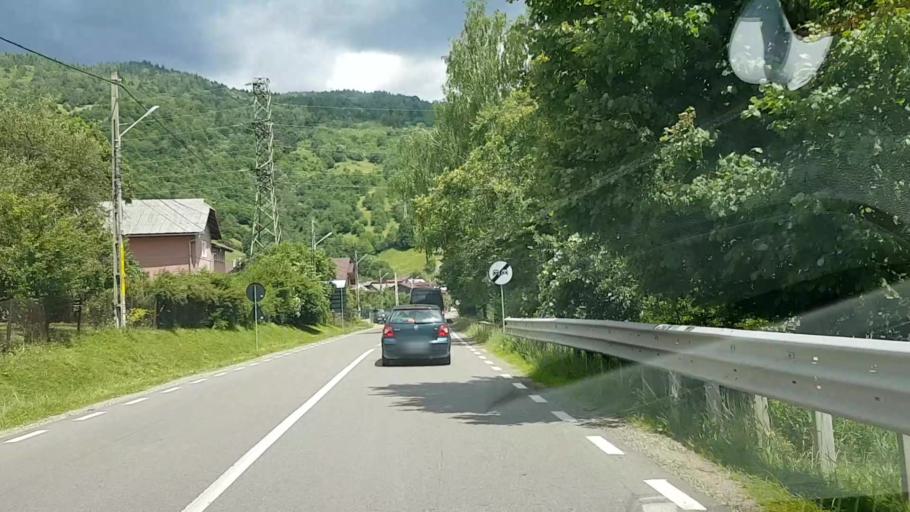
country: RO
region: Suceava
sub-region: Comuna Brosteni
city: Brosteni
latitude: 47.2597
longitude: 25.6825
